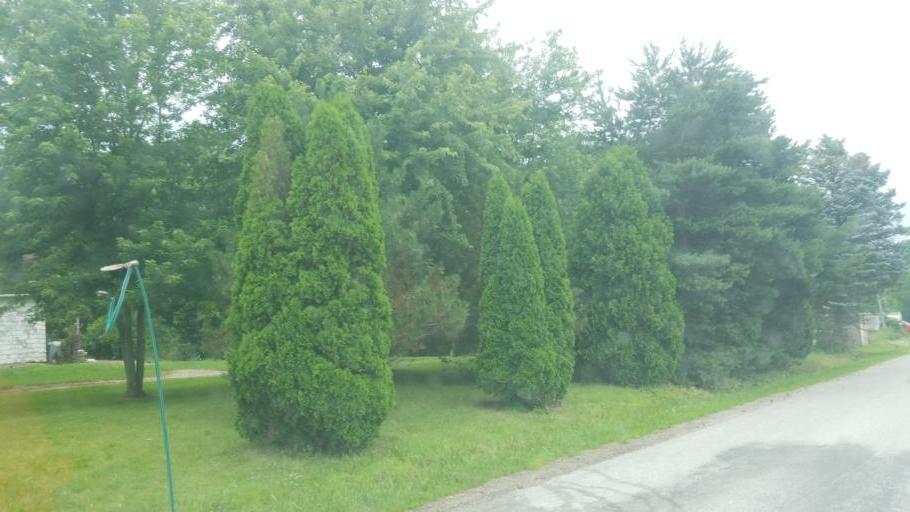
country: US
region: Ohio
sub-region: Wayne County
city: Wooster
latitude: 40.8945
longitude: -81.9533
